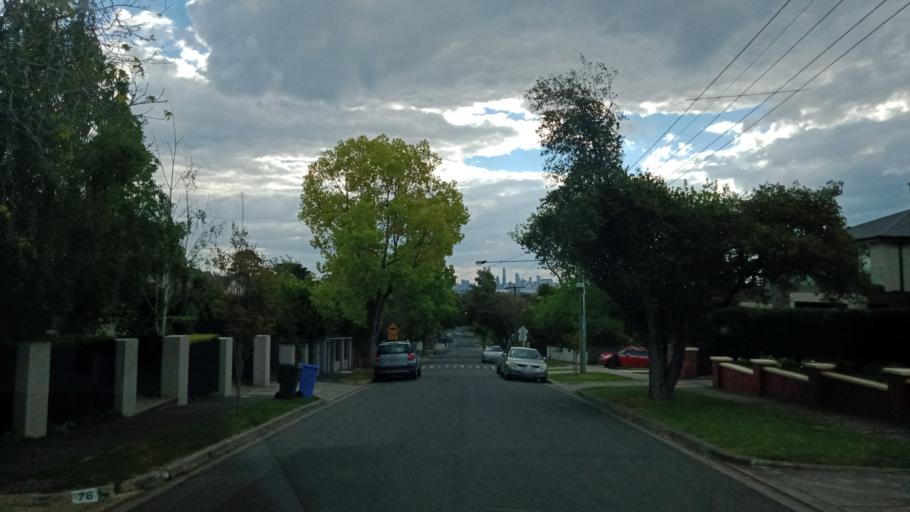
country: AU
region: Victoria
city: Glenferrie
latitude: -37.8368
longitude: 145.0535
